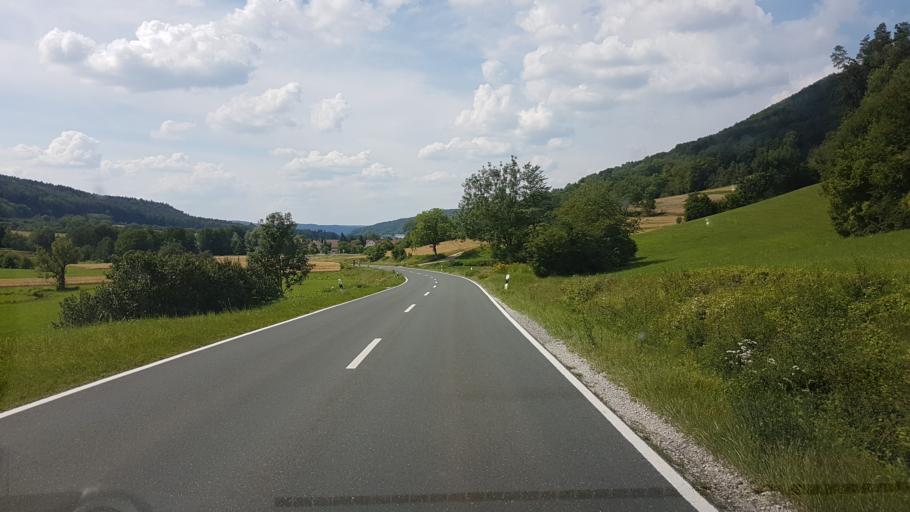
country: DE
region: Bavaria
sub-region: Upper Franconia
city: Egloffstein
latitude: 49.7348
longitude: 11.2296
